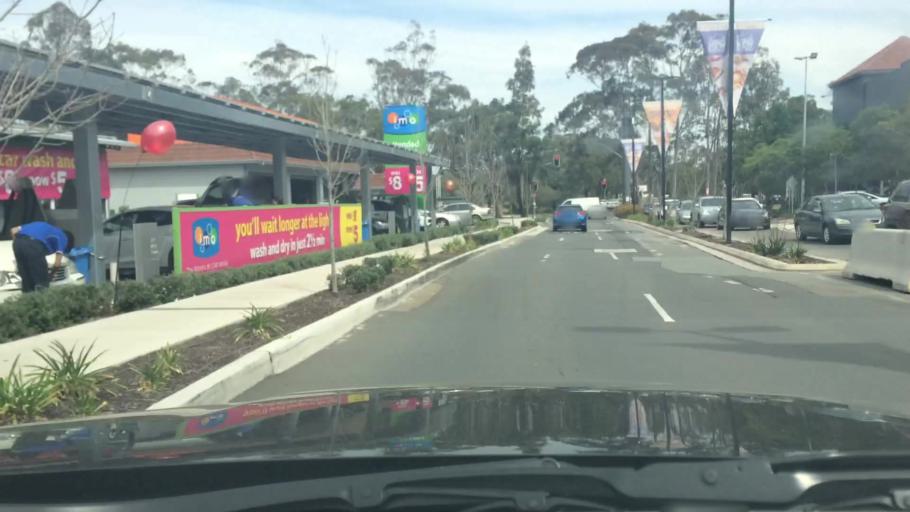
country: AU
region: New South Wales
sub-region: Fairfield
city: Cabramatta West
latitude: -33.8599
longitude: 150.8997
